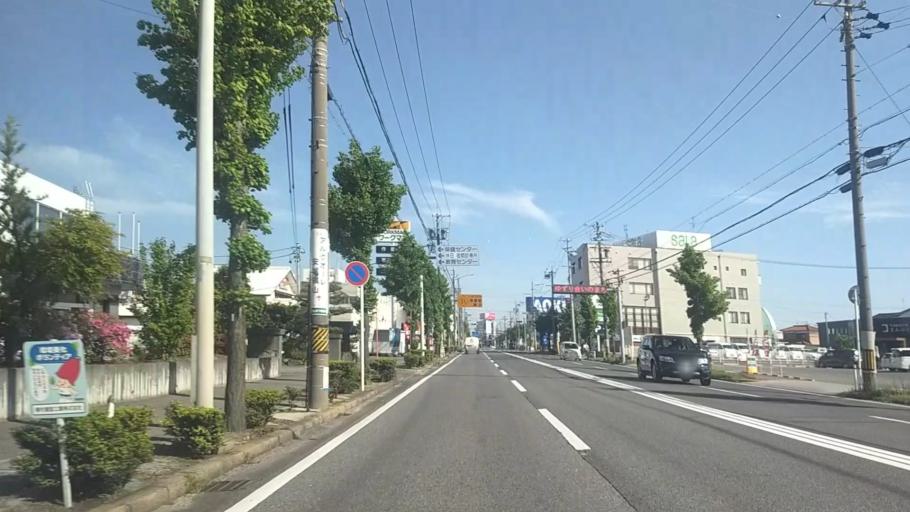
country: JP
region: Aichi
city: Anjo
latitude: 34.9599
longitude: 137.0716
